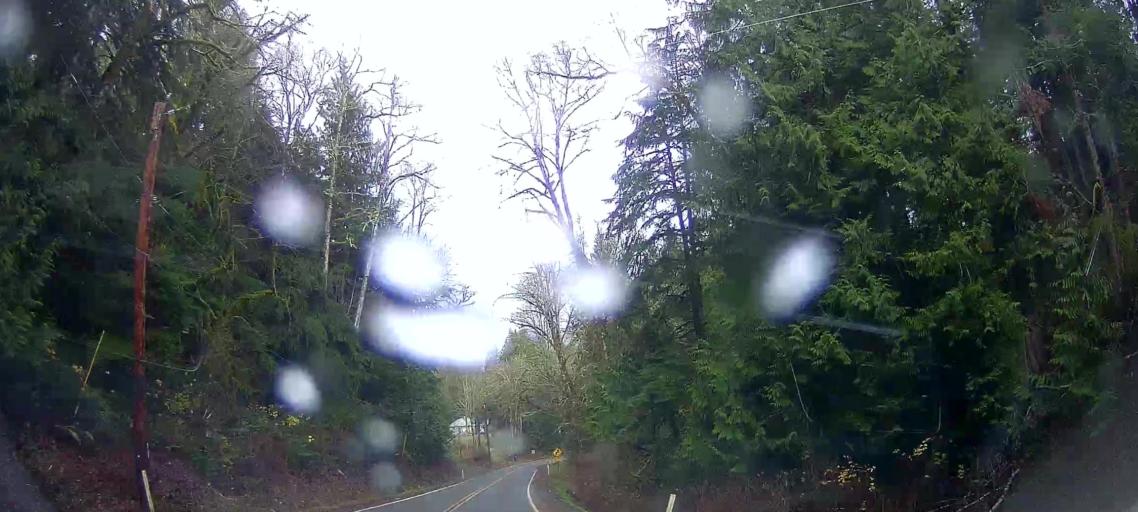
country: US
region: Washington
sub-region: Skagit County
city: Clear Lake
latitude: 48.4815
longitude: -122.1377
